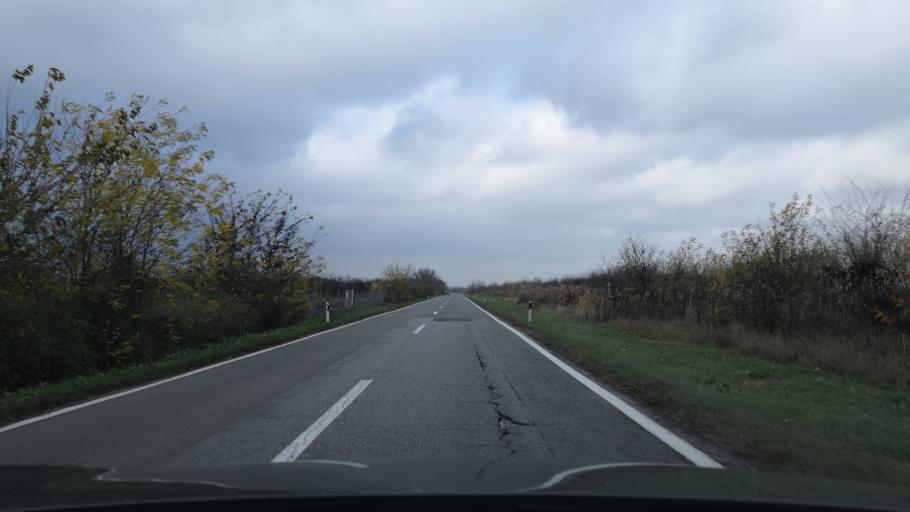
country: RS
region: Autonomna Pokrajina Vojvodina
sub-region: Severnobanatski Okrug
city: Coka
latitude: 45.9575
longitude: 20.1342
